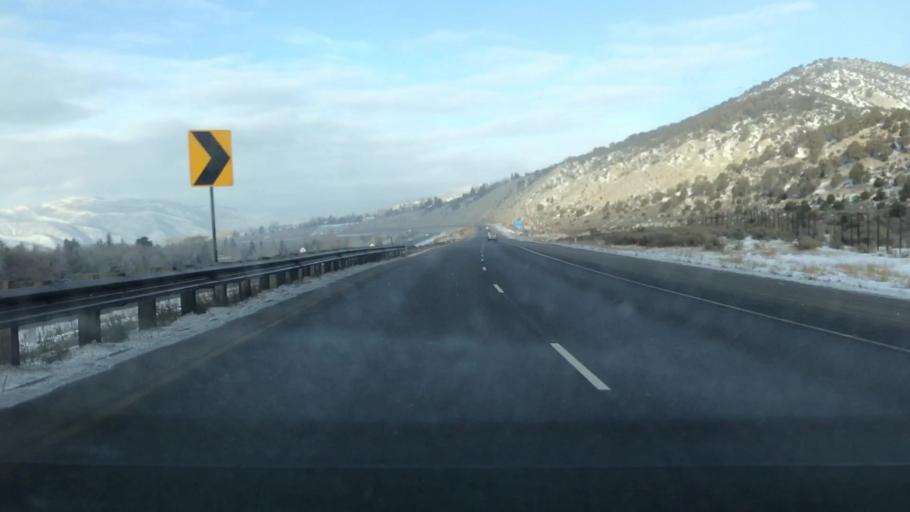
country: US
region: Colorado
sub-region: Eagle County
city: Avon
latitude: 39.6388
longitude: -106.5479
